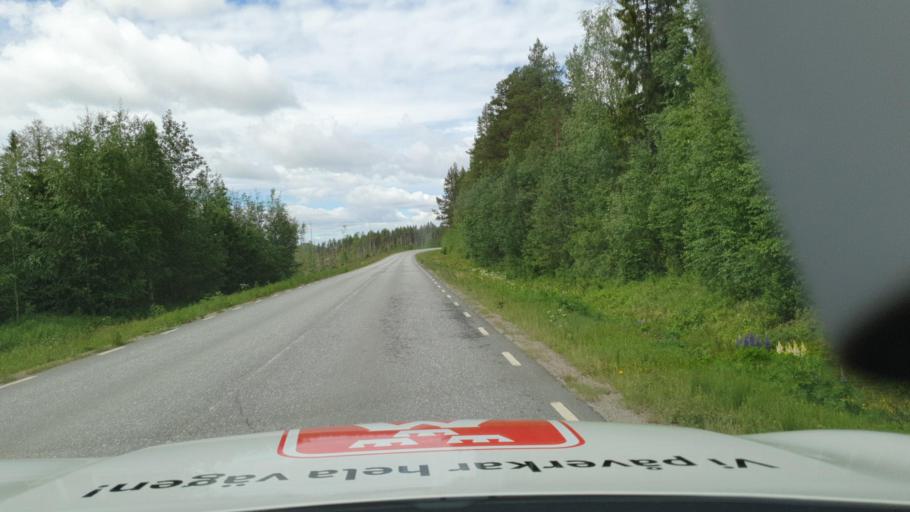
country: SE
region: Vaesterbotten
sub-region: Dorotea Kommun
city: Dorotea
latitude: 64.2669
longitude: 16.3518
